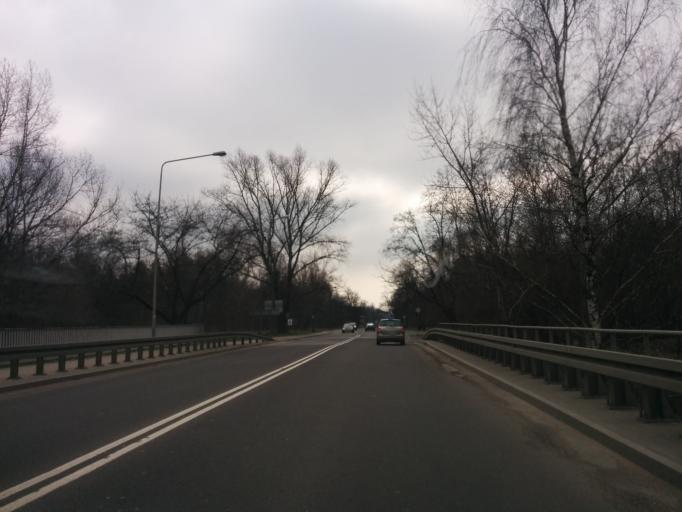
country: PL
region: Masovian Voivodeship
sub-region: Warszawa
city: Bialoleka
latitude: 52.3129
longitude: 21.0022
